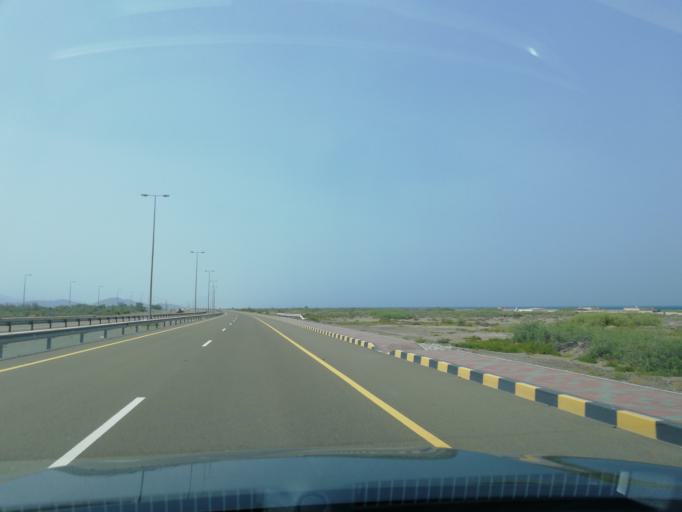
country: OM
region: Al Batinah
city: Shinas
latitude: 24.8874
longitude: 56.4023
